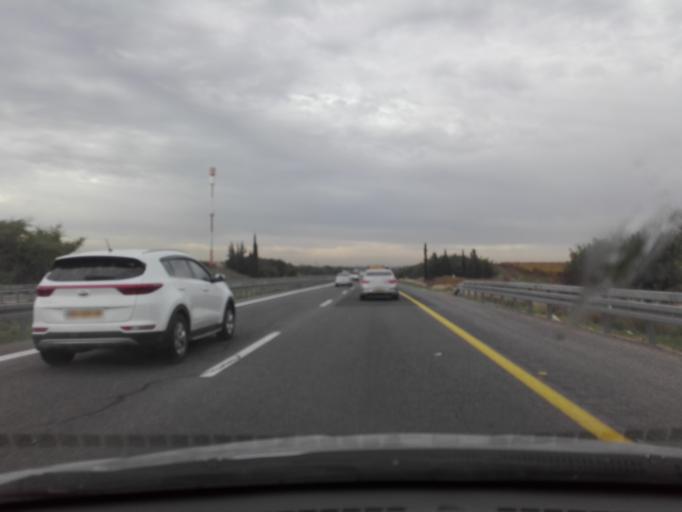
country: IL
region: Central District
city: Mazkeret Batya
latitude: 31.8668
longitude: 34.8737
